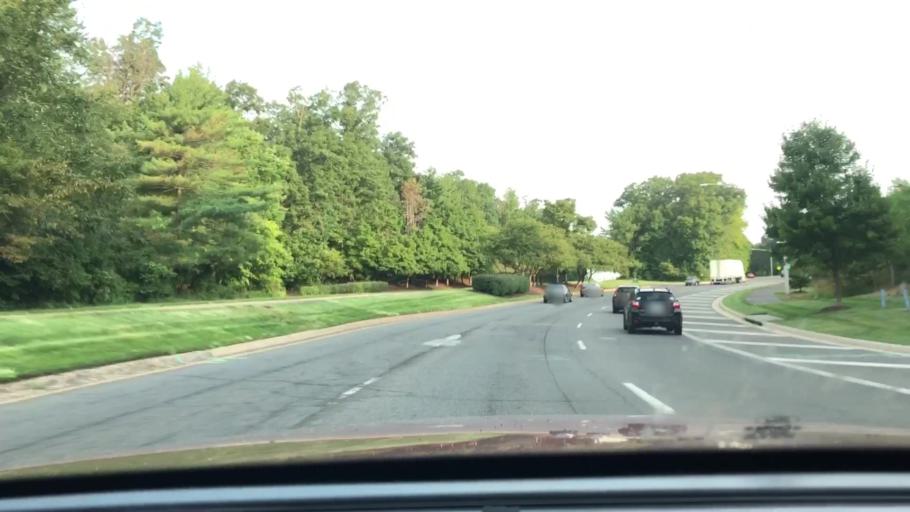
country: US
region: Virginia
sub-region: Fairfax County
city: Chantilly
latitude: 38.8728
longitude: -77.4535
